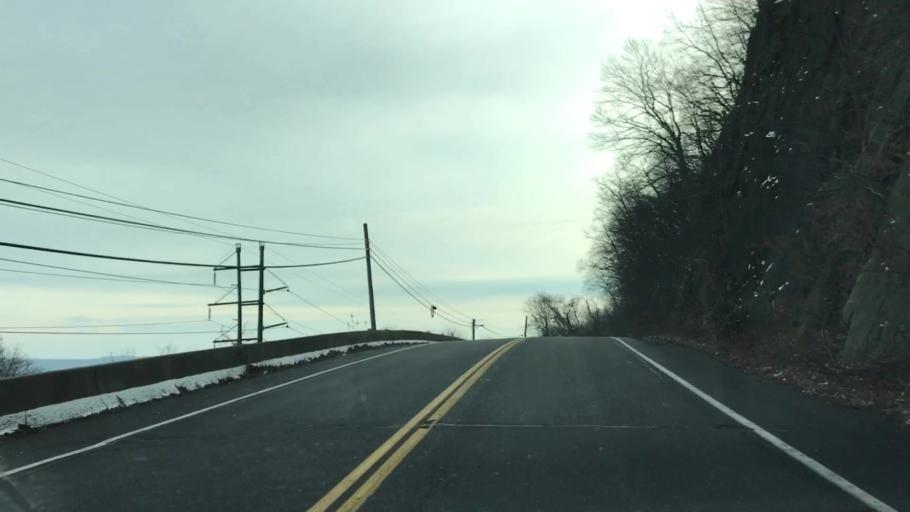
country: US
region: New York
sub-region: Rockland County
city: Haverstraw
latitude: 41.1815
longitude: -73.9532
